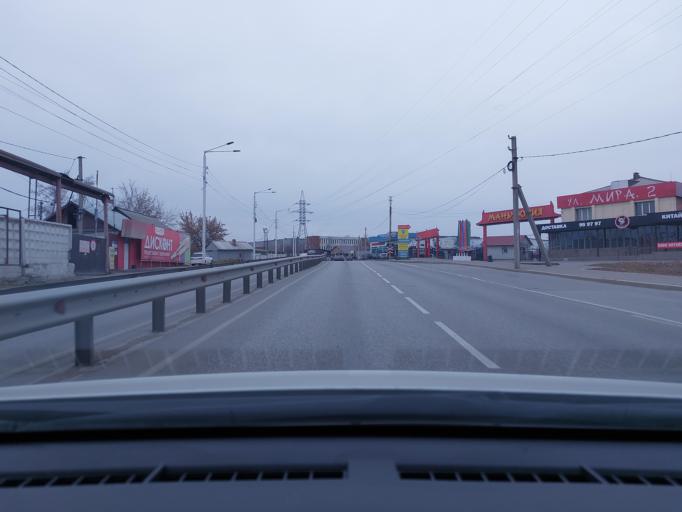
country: RU
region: Irkutsk
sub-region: Irkutskiy Rayon
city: Irkutsk
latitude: 52.3370
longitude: 104.2330
